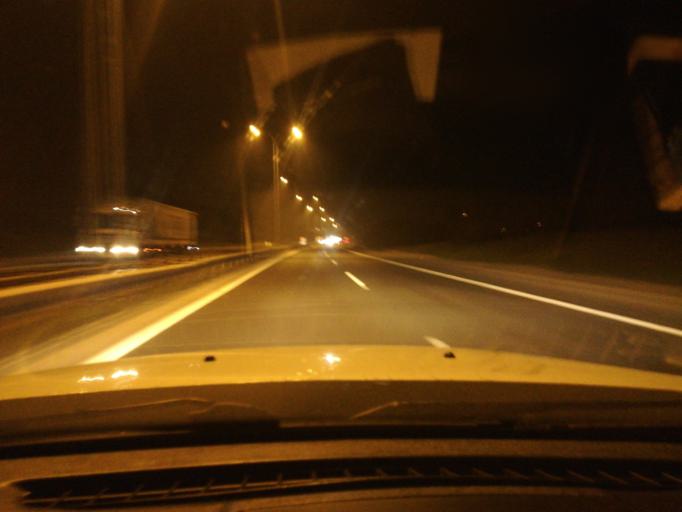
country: TR
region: Istanbul
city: Celaliye
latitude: 41.0557
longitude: 28.4248
